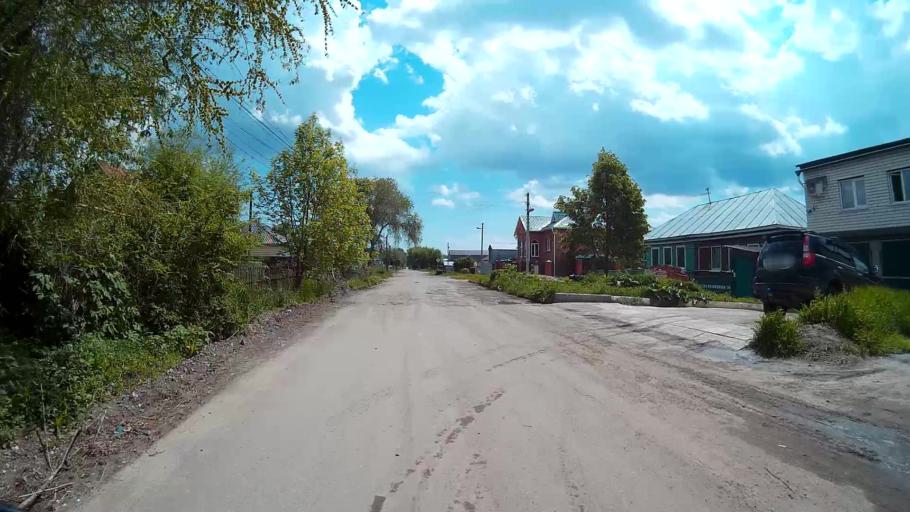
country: RU
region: Ulyanovsk
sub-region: Ulyanovskiy Rayon
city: Ulyanovsk
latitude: 54.3468
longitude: 48.3584
